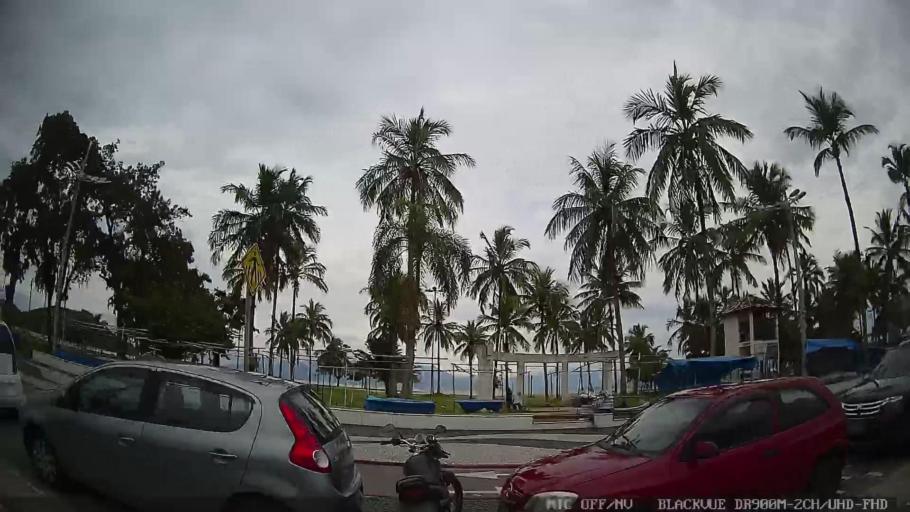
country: BR
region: Sao Paulo
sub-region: Caraguatatuba
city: Caraguatatuba
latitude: -23.6231
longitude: -45.4080
